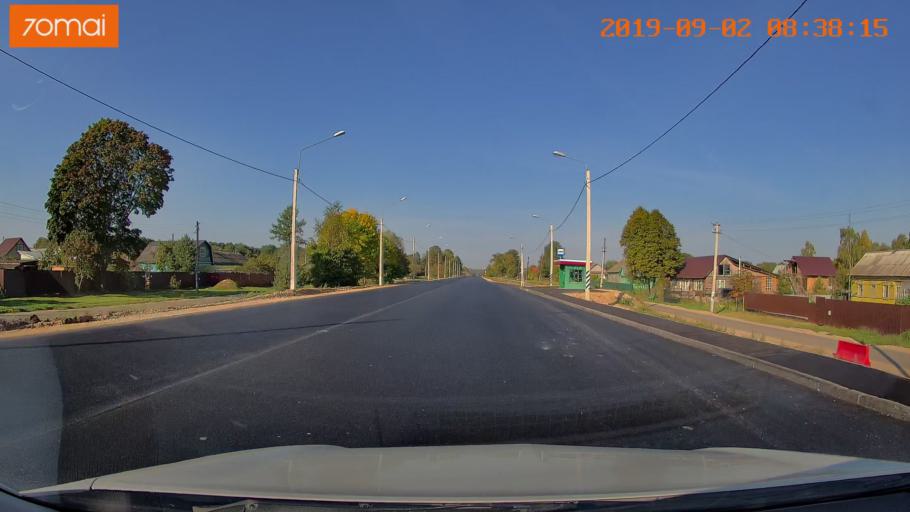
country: RU
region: Kaluga
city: Kudinovo
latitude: 54.9779
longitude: 36.1823
